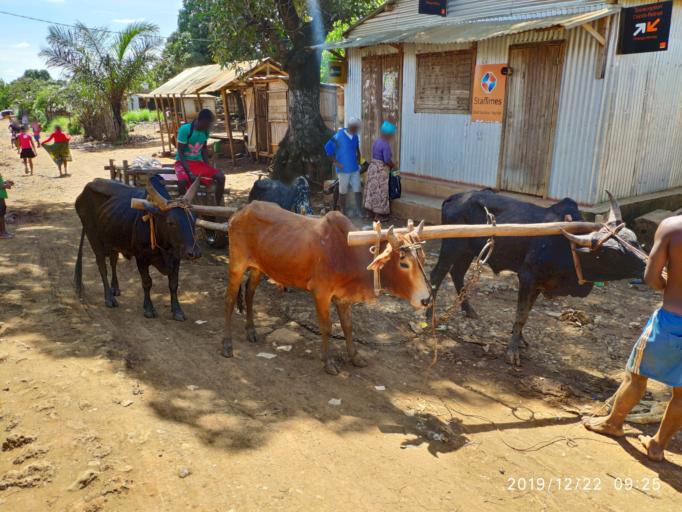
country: MG
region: Diana
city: Sadjoavato
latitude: -12.7418
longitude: 49.2344
